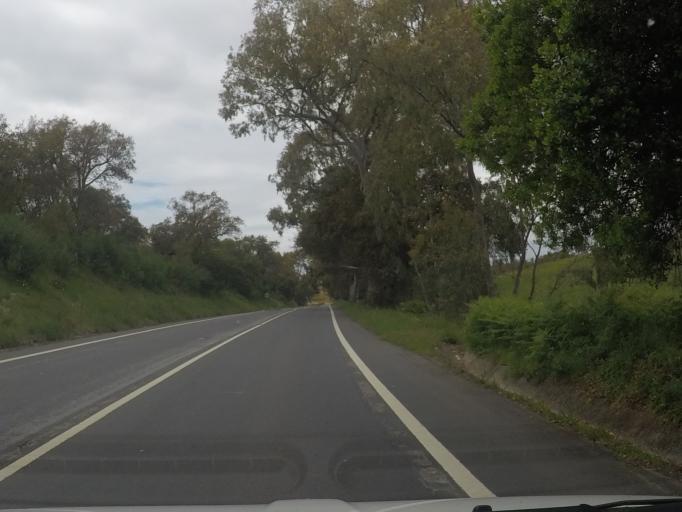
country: PT
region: Setubal
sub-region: Santiago do Cacem
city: Cercal
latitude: 37.8327
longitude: -8.7025
